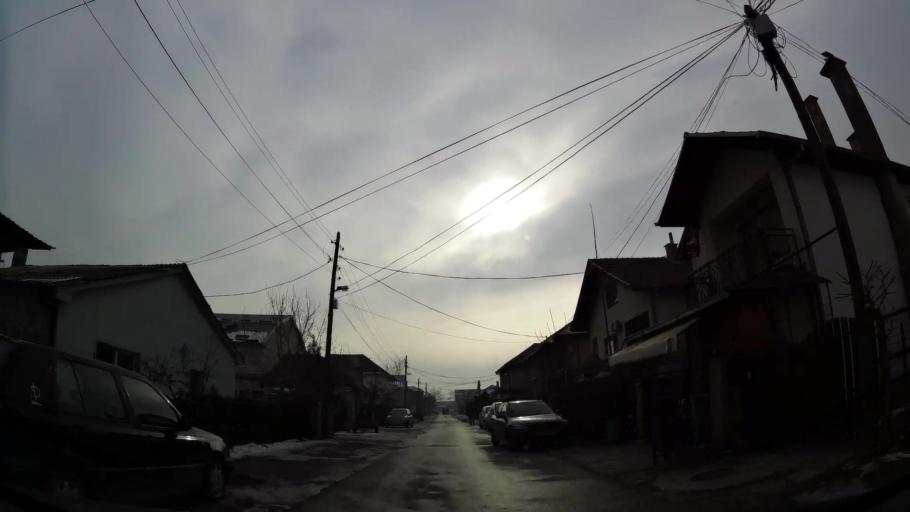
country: MK
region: Ilinden
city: Ilinden
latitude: 41.9932
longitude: 21.5845
